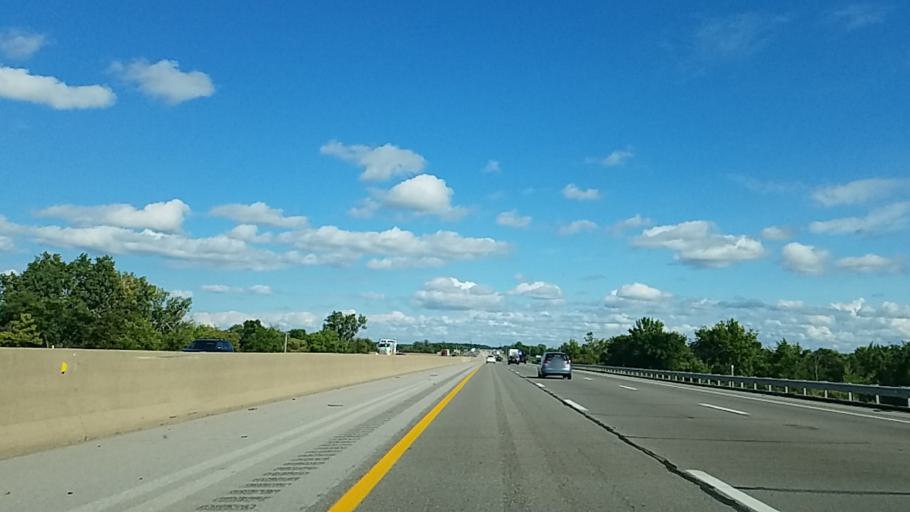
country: US
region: Ohio
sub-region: Sandusky County
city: Clyde
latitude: 41.3730
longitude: -82.9760
